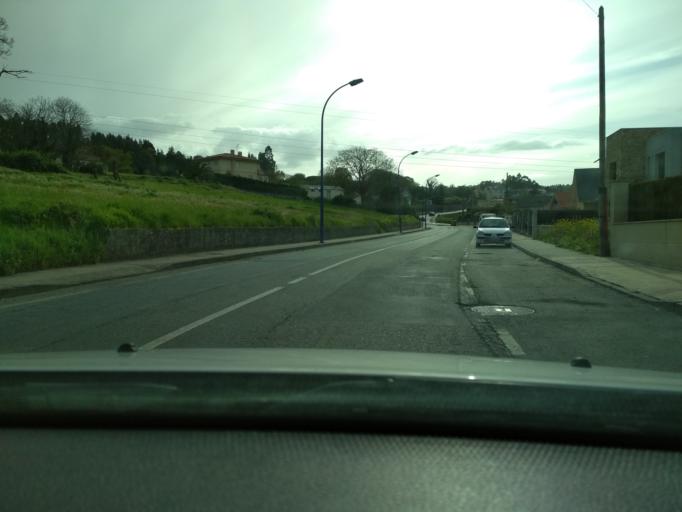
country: ES
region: Galicia
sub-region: Provincia da Coruna
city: Culleredo
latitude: 43.2872
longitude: -8.3838
